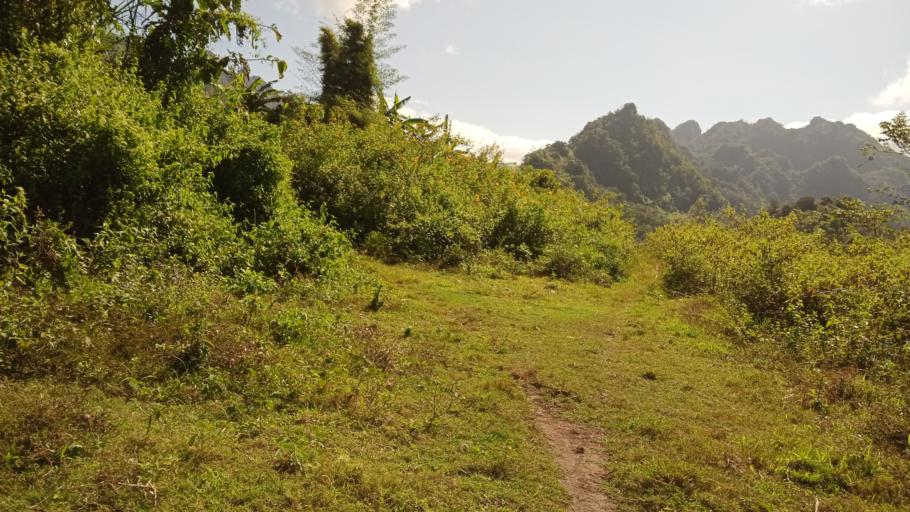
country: LA
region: Xiangkhoang
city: Phonsavan
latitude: 19.1041
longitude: 102.9311
